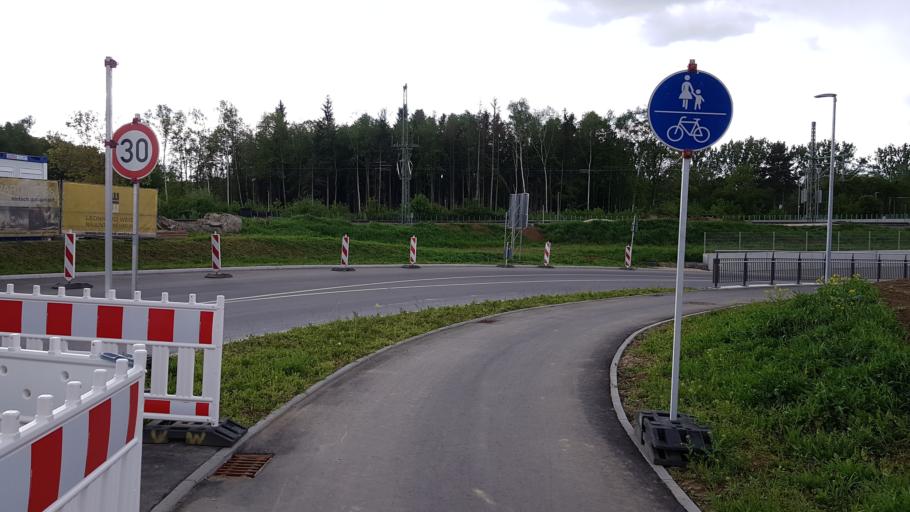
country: DE
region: Baden-Wuerttemberg
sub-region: Regierungsbezirk Stuttgart
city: Wendlingen am Neckar
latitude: 48.6666
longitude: 9.3695
